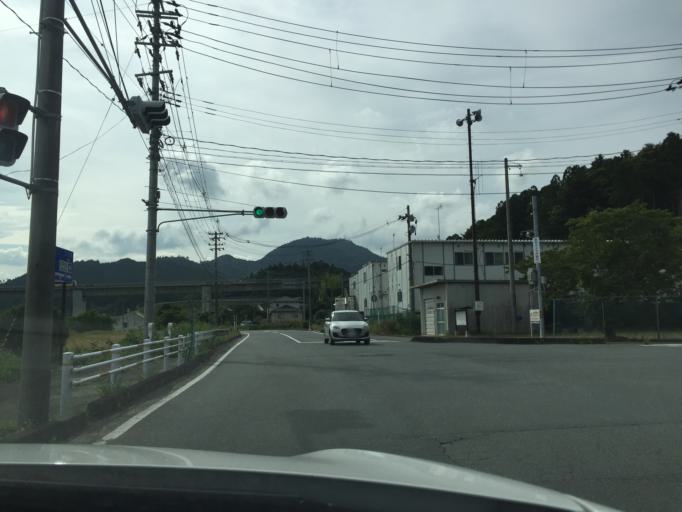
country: JP
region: Fukushima
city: Namie
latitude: 37.2829
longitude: 140.9843
